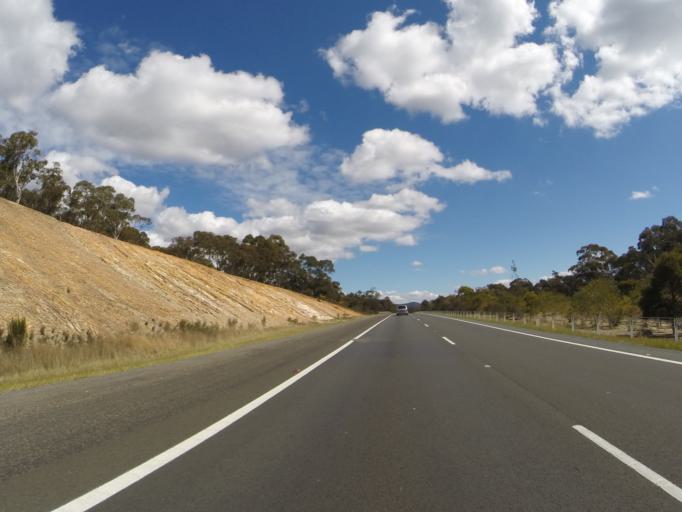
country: AU
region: New South Wales
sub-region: Goulburn Mulwaree
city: Goulburn
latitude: -34.7425
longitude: 149.9041
